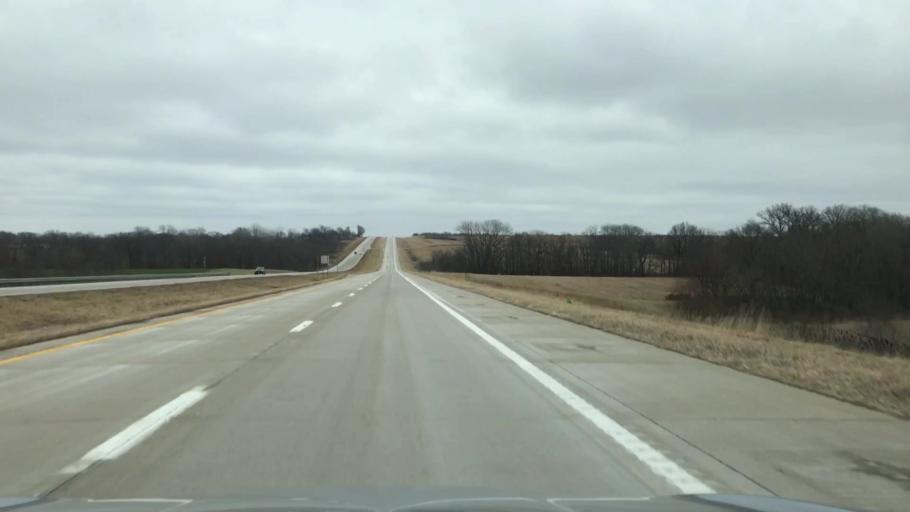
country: US
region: Missouri
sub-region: Livingston County
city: Chillicothe
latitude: 39.7377
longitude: -93.7037
